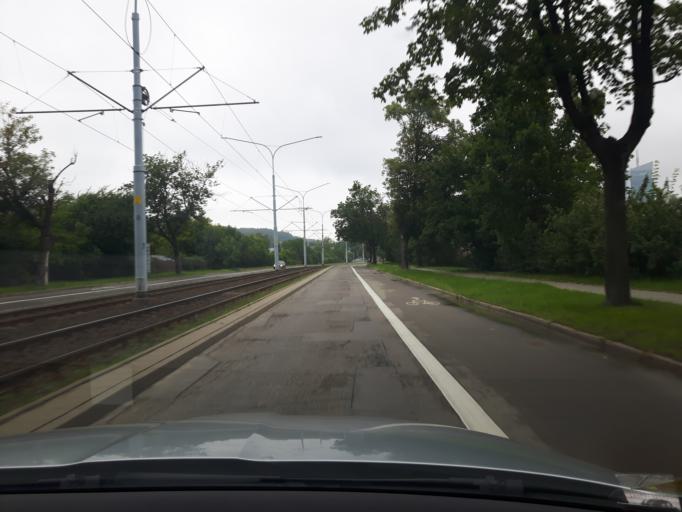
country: PL
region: Pomeranian Voivodeship
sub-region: Sopot
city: Sopot
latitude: 54.3939
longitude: 18.5740
